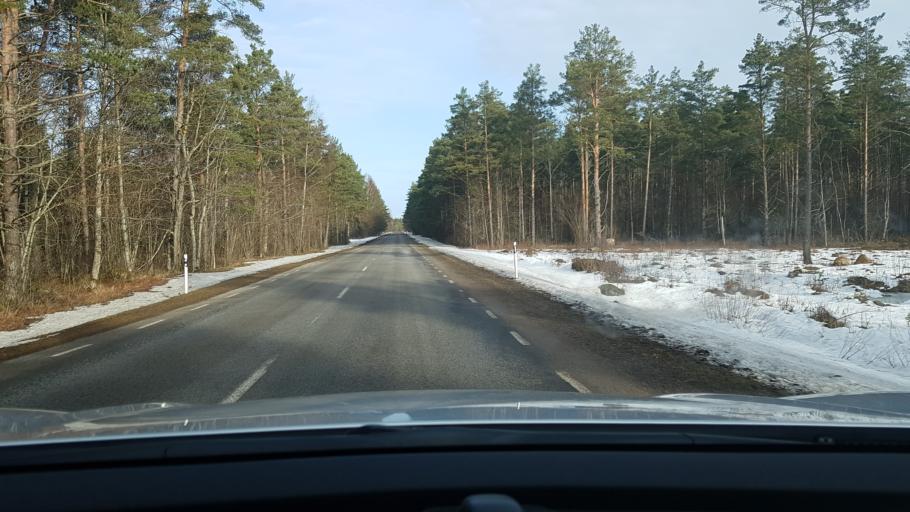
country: EE
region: Saare
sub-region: Kuressaare linn
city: Kuressaare
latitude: 58.4718
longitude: 22.7028
